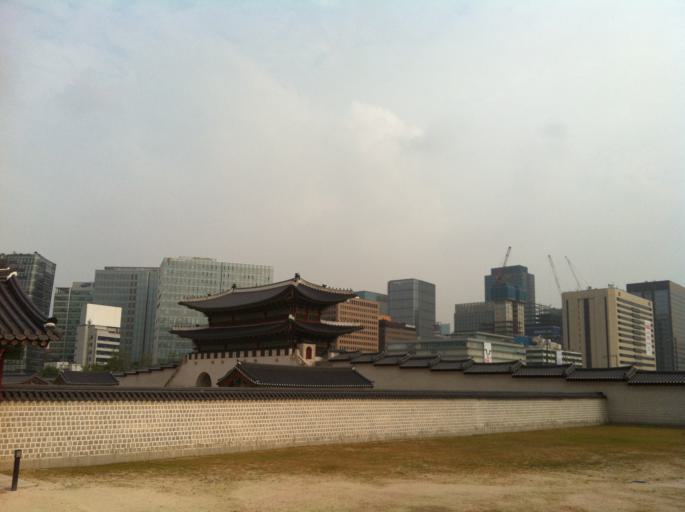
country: KR
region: Seoul
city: Seoul
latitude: 37.5765
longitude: 126.9758
